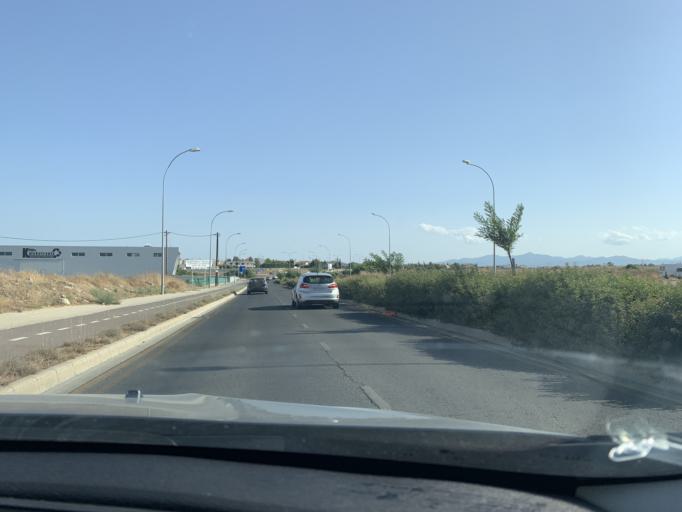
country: CY
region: Lefkosia
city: Tseri
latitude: 35.1183
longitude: 33.3567
